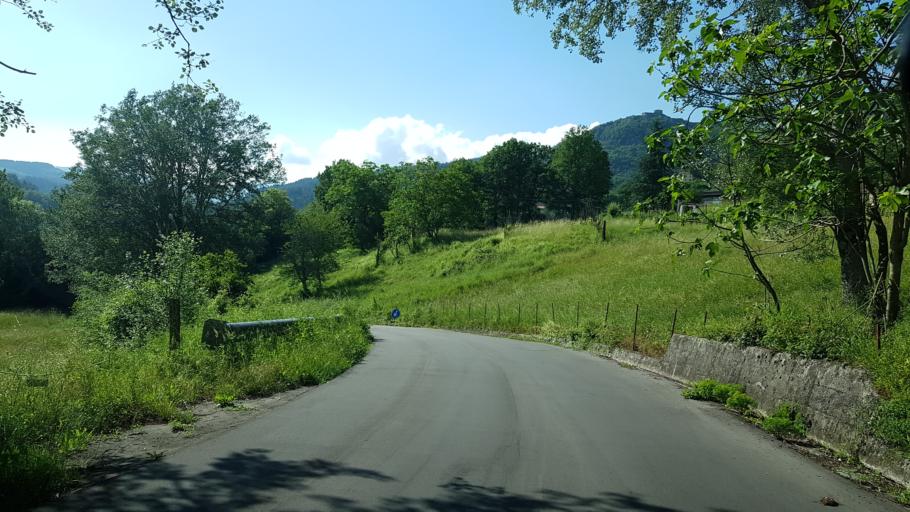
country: IT
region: Tuscany
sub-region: Provincia di Lucca
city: San Romano in Garfagnana
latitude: 44.1662
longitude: 10.3422
